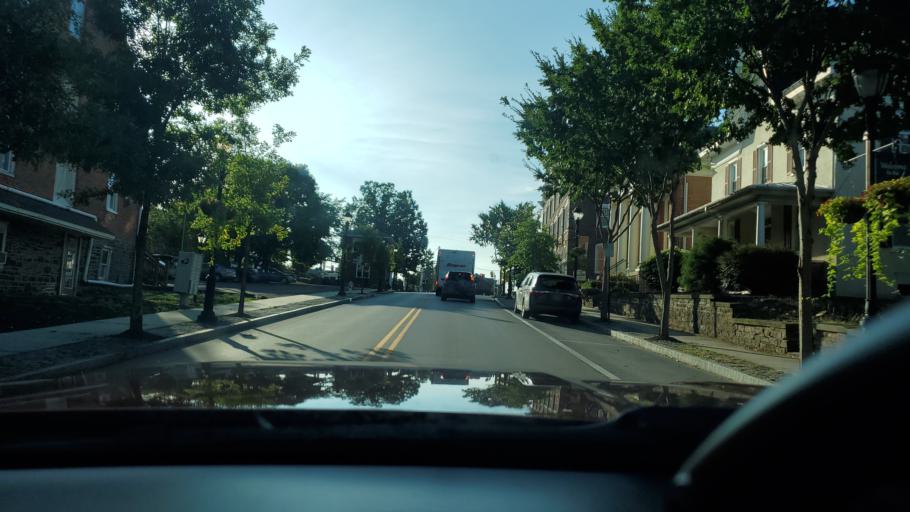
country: US
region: Pennsylvania
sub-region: Montgomery County
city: Souderton
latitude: 40.3101
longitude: -75.3222
